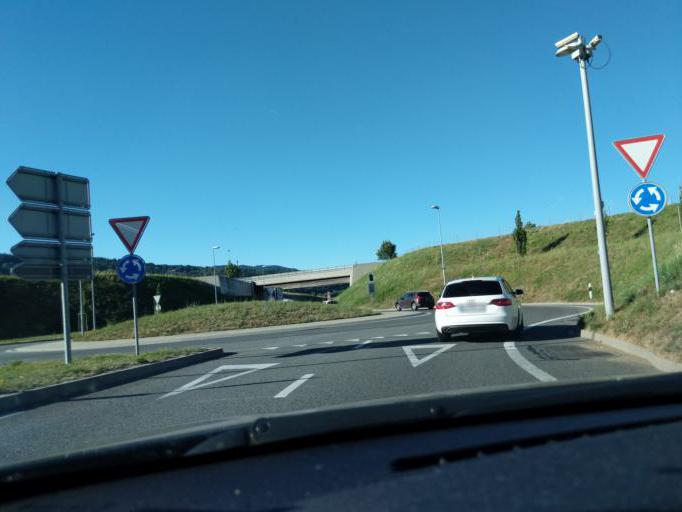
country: CH
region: Fribourg
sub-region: Gruyere District
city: Bulle
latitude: 46.6255
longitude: 7.0431
